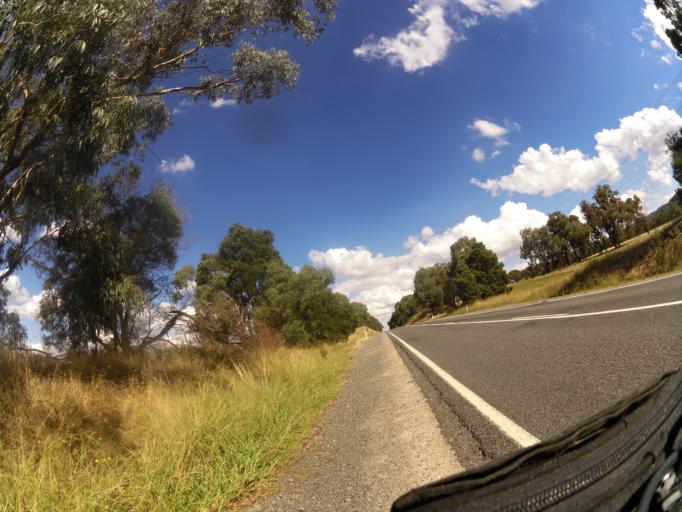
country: AU
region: Victoria
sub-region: Mansfield
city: Mansfield
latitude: -36.8854
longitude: 145.9949
